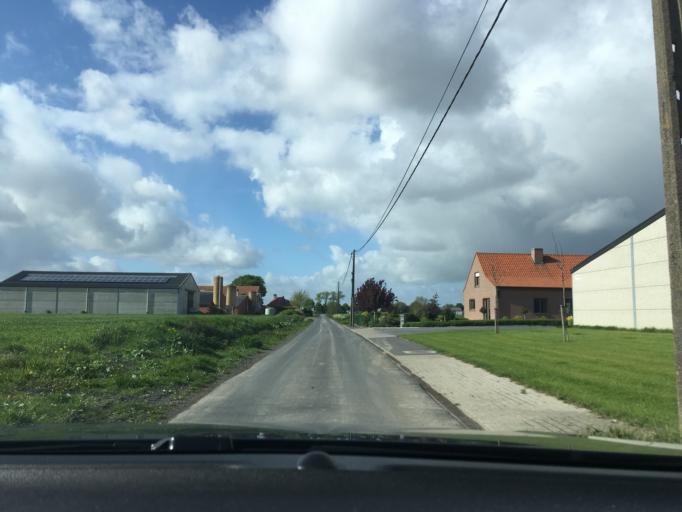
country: BE
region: Flanders
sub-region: Provincie West-Vlaanderen
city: Hooglede
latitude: 50.9944
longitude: 3.0631
